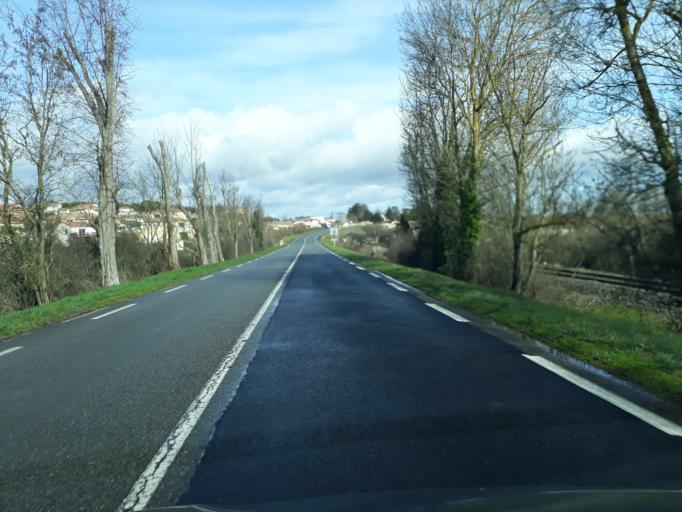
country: FR
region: Midi-Pyrenees
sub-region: Departement du Gers
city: Pujaudran
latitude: 43.6101
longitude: 1.0587
